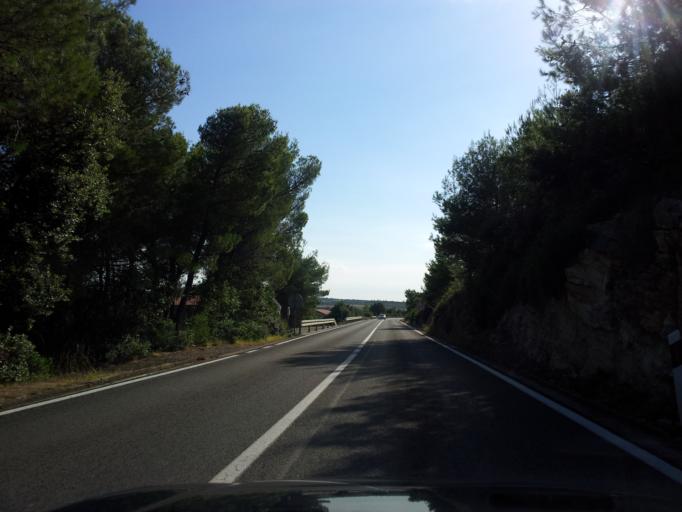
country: HR
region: Zadarska
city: Posedarje
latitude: 44.2130
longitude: 15.4969
